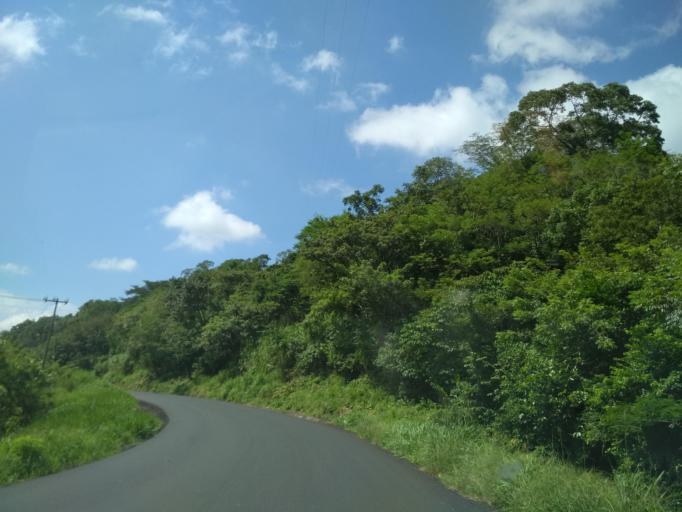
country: MX
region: Veracruz
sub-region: San Andres Tuxtla
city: Texcaltitan Xoteapan (Texcaltitan)
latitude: 18.4436
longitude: -95.2521
